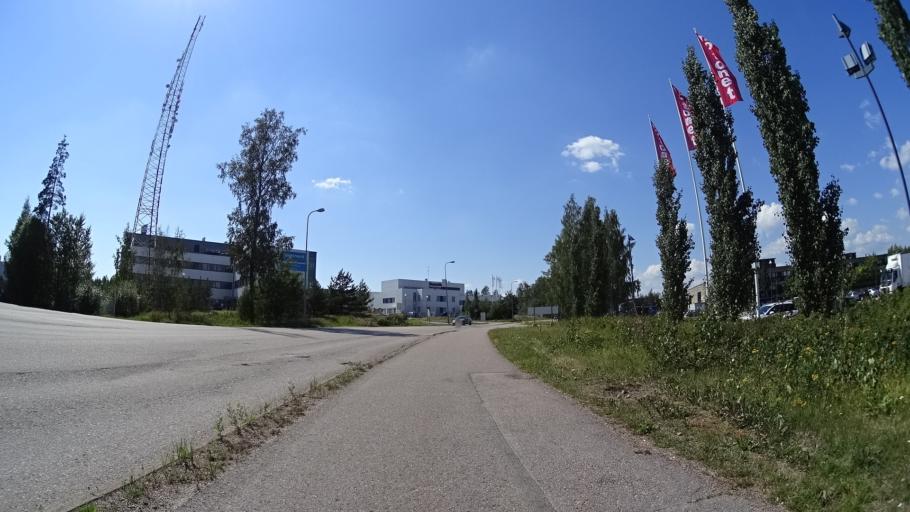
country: FI
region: Uusimaa
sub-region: Helsinki
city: Vantaa
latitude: 60.2957
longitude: 24.9294
